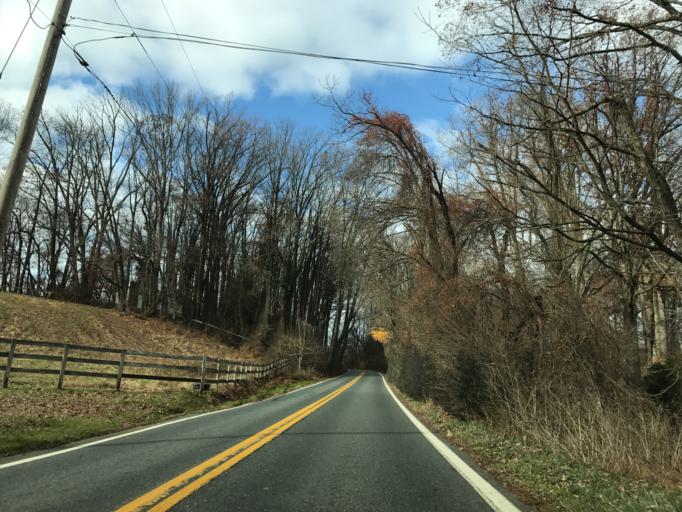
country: US
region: Maryland
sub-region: Baltimore County
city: Perry Hall
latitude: 39.4874
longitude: -76.5100
